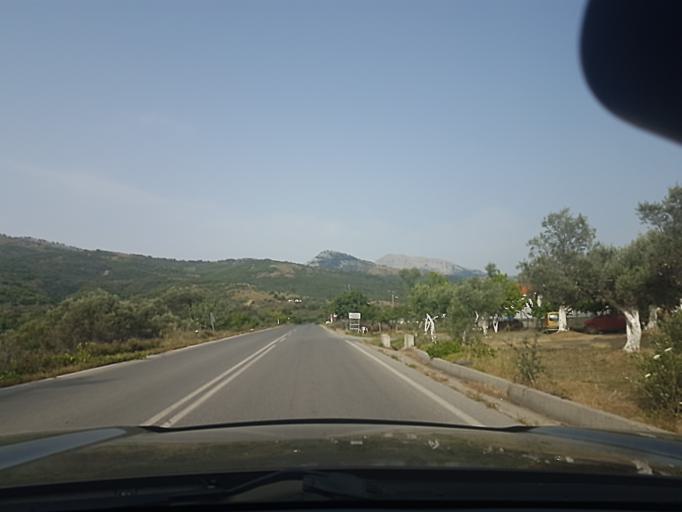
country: GR
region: Central Greece
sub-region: Nomos Evvoias
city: Yimnon
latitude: 38.5754
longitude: 23.8062
